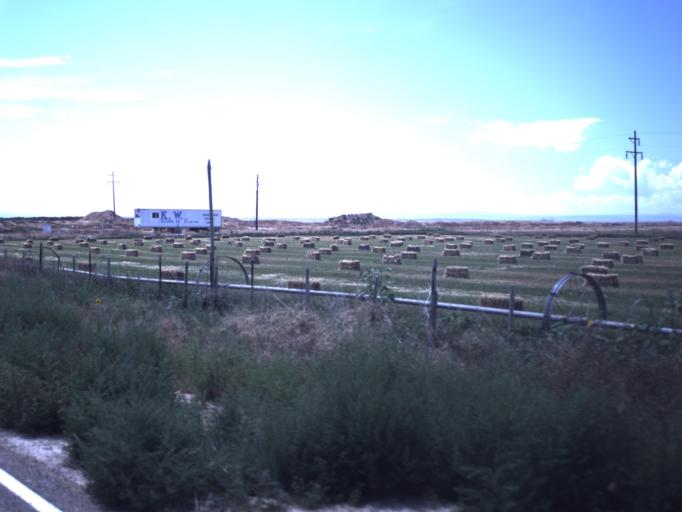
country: US
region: Utah
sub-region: Uintah County
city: Maeser
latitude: 40.2299
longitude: -109.6844
